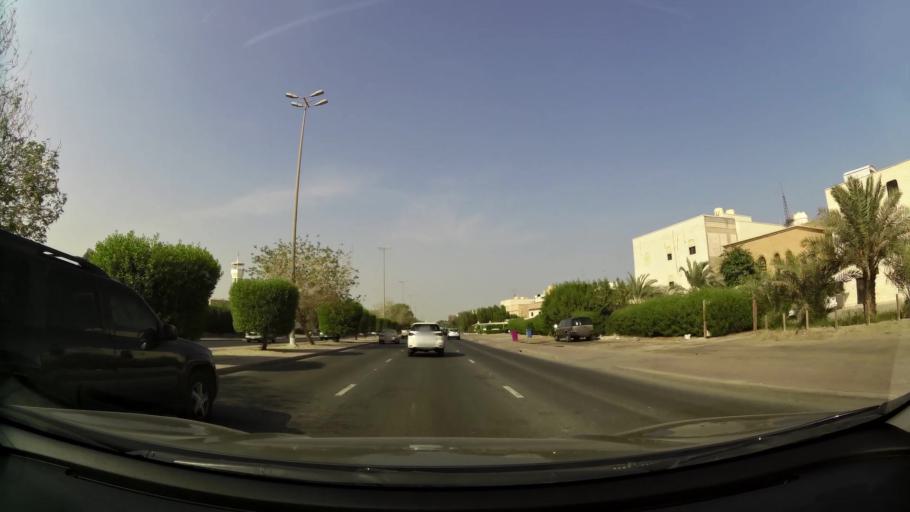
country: KW
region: Al Ahmadi
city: Ar Riqqah
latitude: 29.1623
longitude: 48.0855
